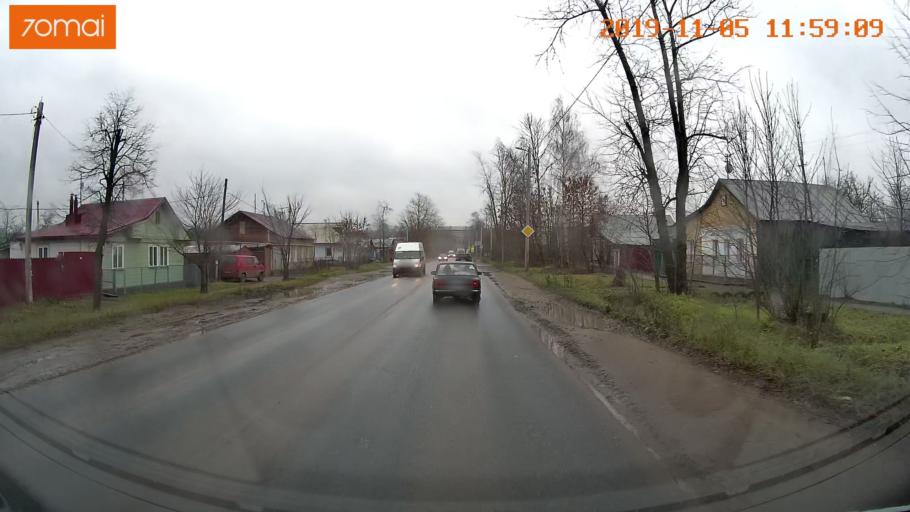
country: RU
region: Ivanovo
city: Kokhma
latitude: 56.9791
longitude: 41.0458
